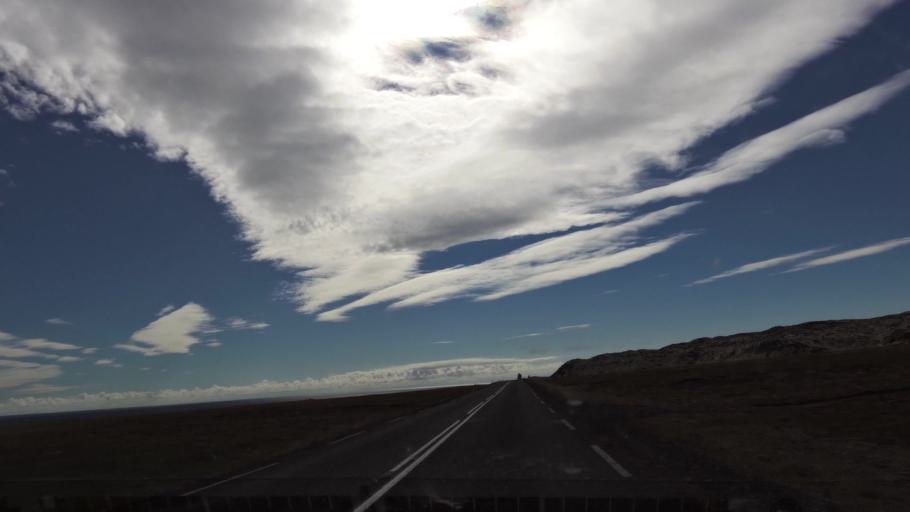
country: IS
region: West
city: Olafsvik
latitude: 64.7477
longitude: -23.7278
